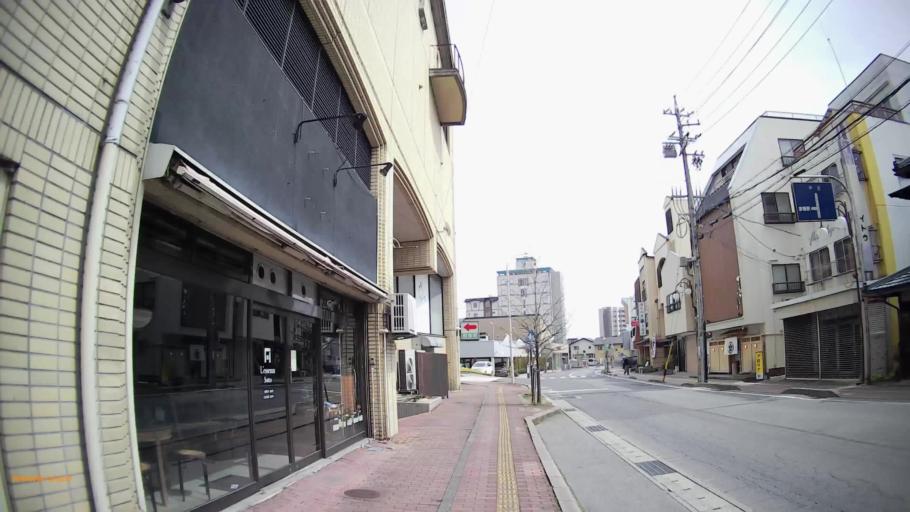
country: JP
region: Nagano
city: Chino
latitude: 35.9937
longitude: 138.1516
